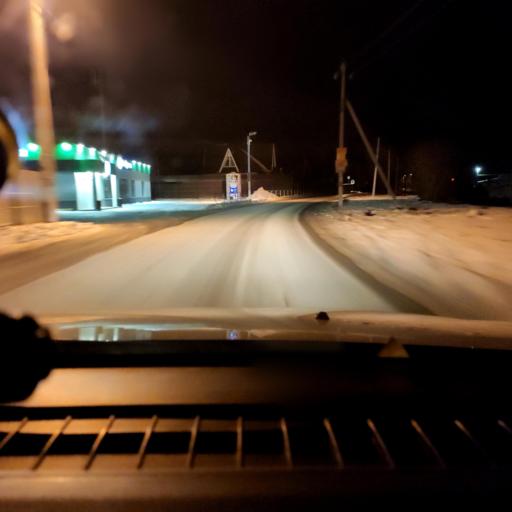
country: RU
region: Samara
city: Novokuybyshevsk
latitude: 53.1453
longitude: 49.9828
